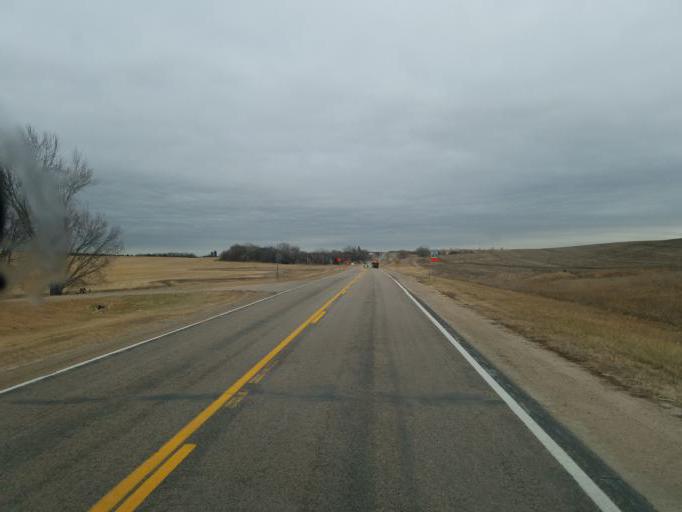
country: US
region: Nebraska
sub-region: Cedar County
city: Hartington
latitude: 42.6127
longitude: -97.4374
